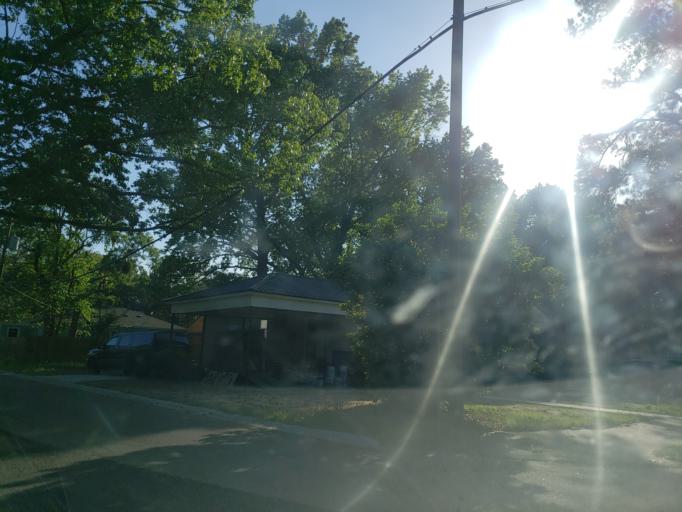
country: US
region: Georgia
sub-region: Chatham County
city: Thunderbolt
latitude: 32.0394
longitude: -81.0867
